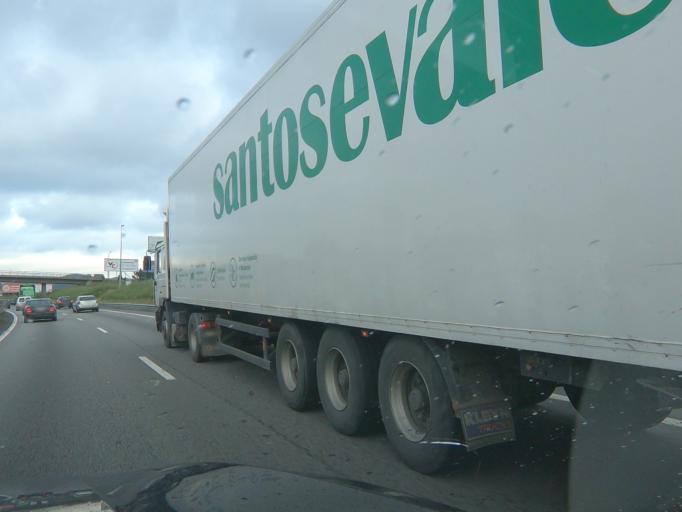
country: PT
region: Porto
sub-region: Maia
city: Pedroucos
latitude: 41.1983
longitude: -8.5725
